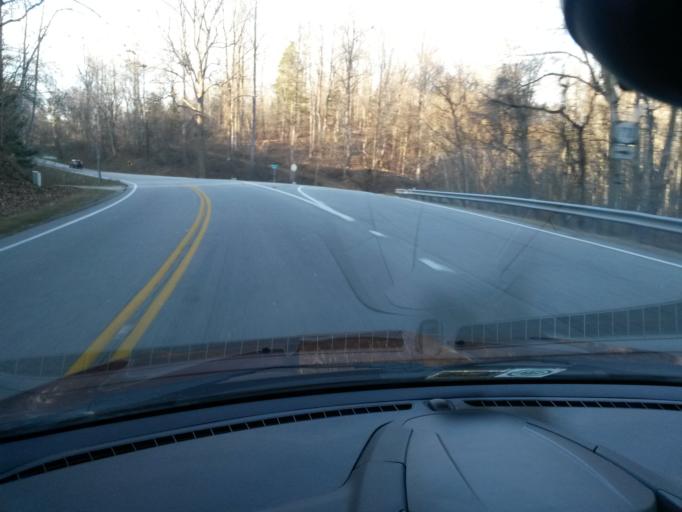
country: US
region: Virginia
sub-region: Amherst County
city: Amherst
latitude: 37.6396
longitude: -79.1185
